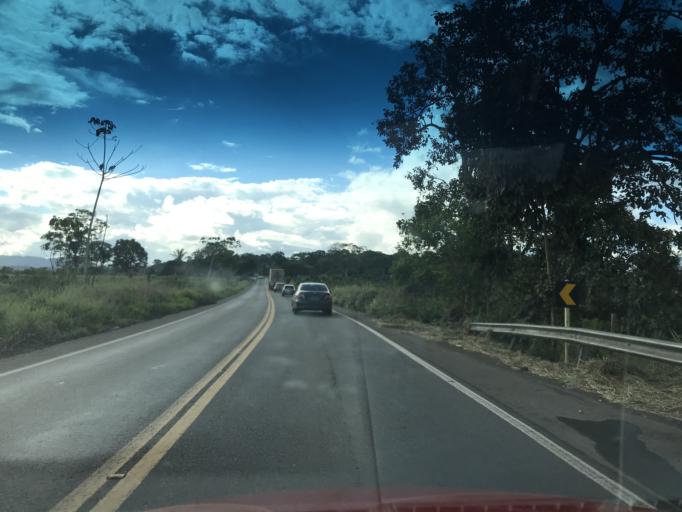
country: BR
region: Bahia
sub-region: Ibirapitanga
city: Ibirapitanga
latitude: -14.1546
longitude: -39.3271
